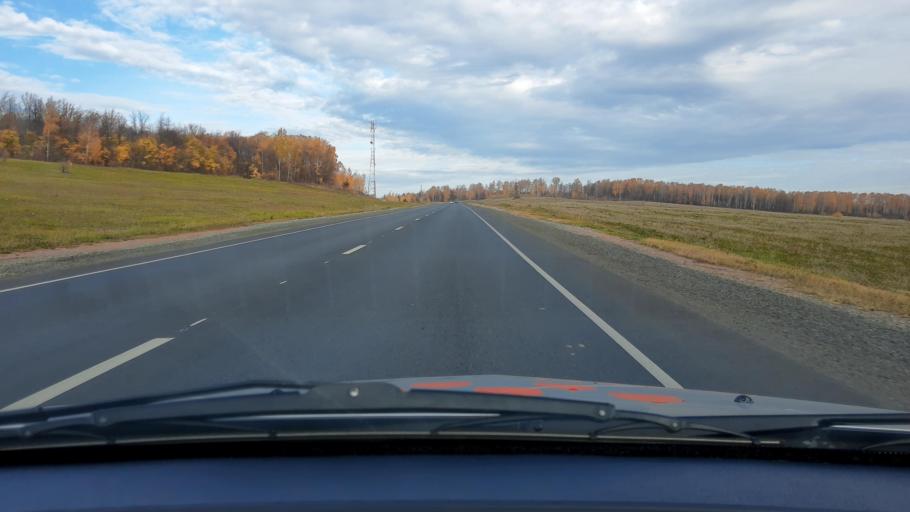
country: RU
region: Bashkortostan
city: Avdon
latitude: 54.8277
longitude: 55.7263
